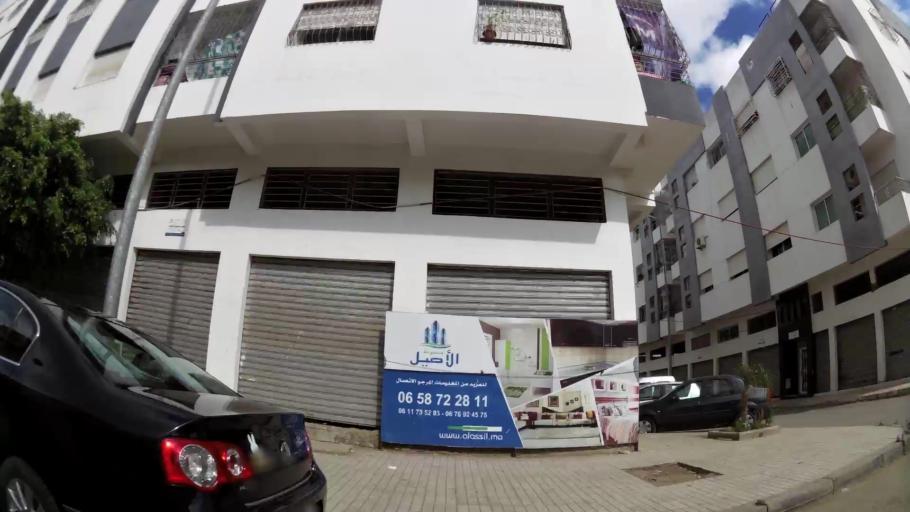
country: MA
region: Gharb-Chrarda-Beni Hssen
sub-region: Kenitra Province
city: Kenitra
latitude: 34.2670
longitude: -6.5660
